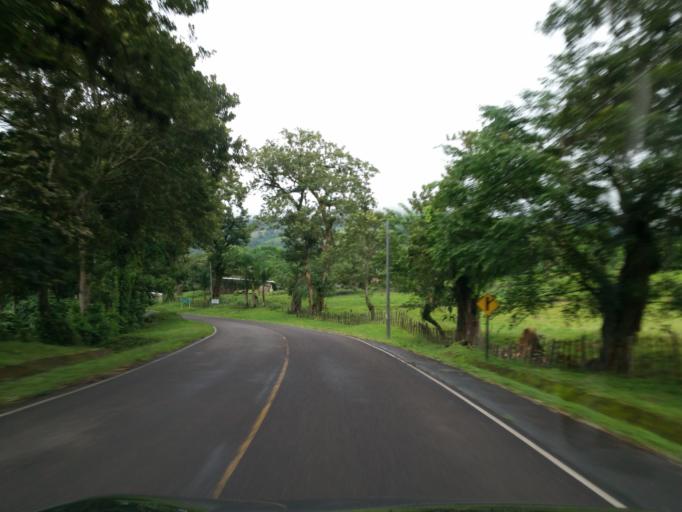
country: NI
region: Matagalpa
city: San Ramon
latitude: 12.9778
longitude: -85.8473
